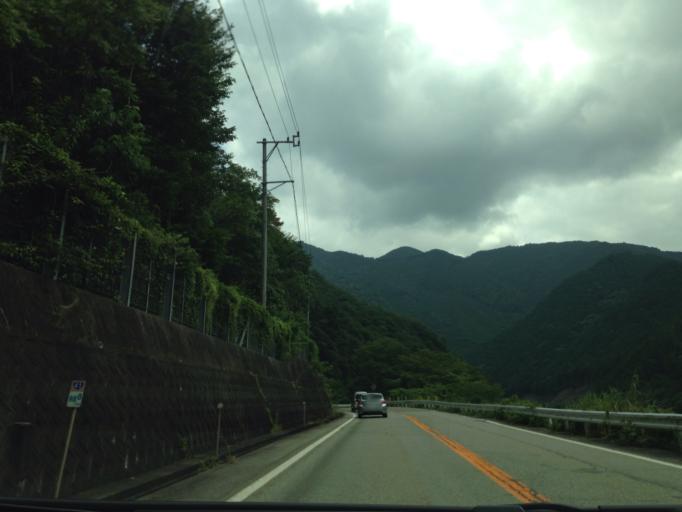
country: JP
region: Gifu
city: Gujo
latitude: 35.7504
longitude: 137.2197
